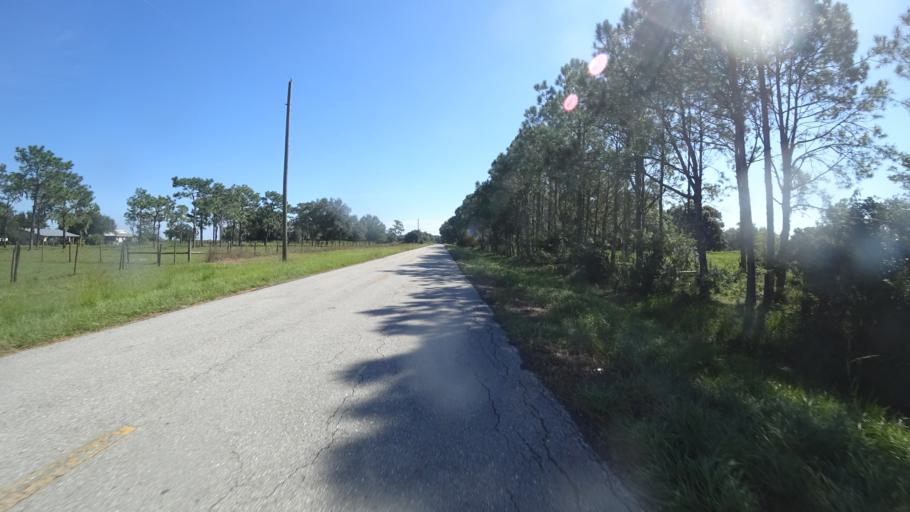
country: US
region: Florida
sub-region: Sarasota County
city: Warm Mineral Springs
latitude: 27.2742
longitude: -82.1186
